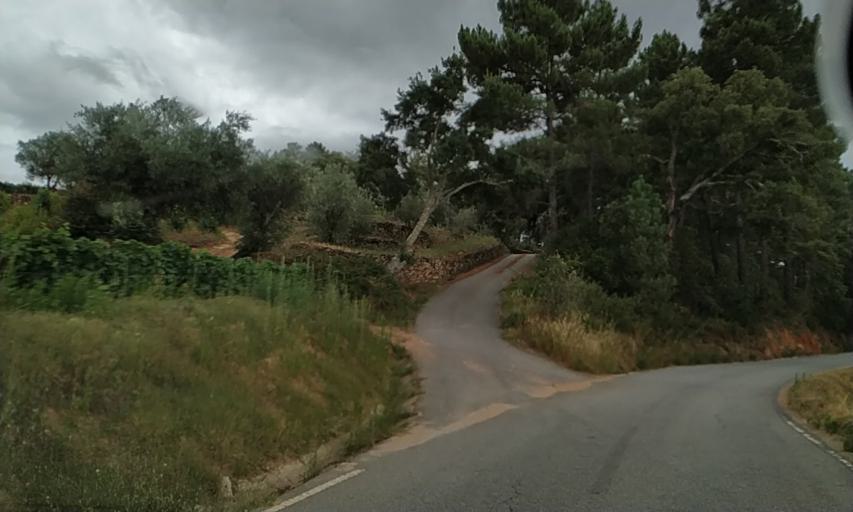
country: PT
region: Vila Real
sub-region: Sabrosa
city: Sabrosa
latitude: 41.2785
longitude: -7.5498
